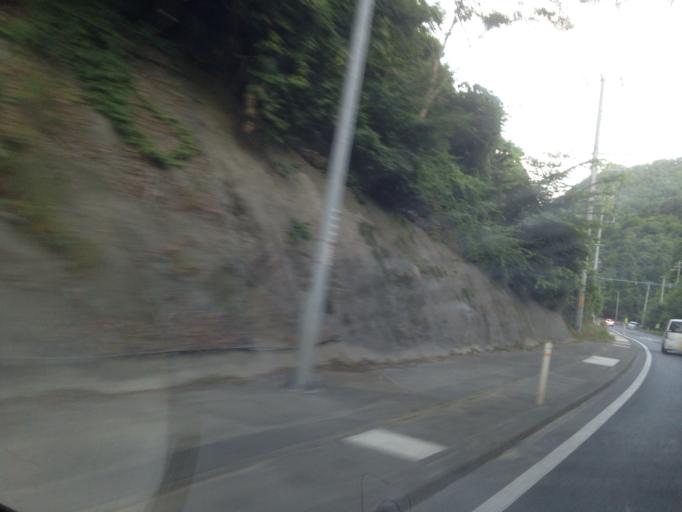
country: JP
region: Iwate
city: Kamaishi
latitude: 39.3149
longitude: 141.8843
